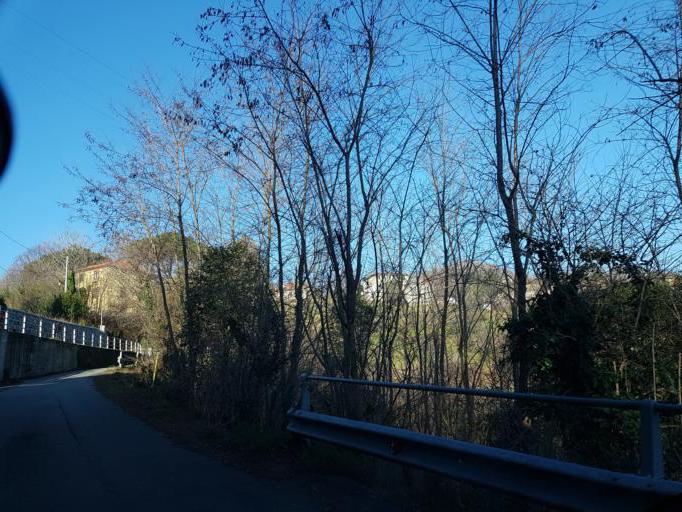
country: IT
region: Liguria
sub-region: Provincia di Genova
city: Santa Marta
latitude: 44.4898
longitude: 8.8905
